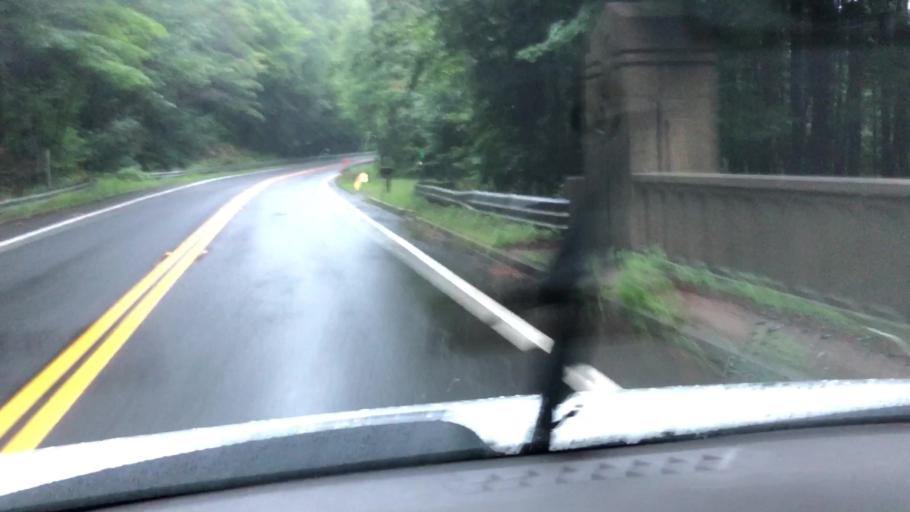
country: US
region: Massachusetts
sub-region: Hampshire County
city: Westhampton
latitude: 42.2835
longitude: -72.8693
